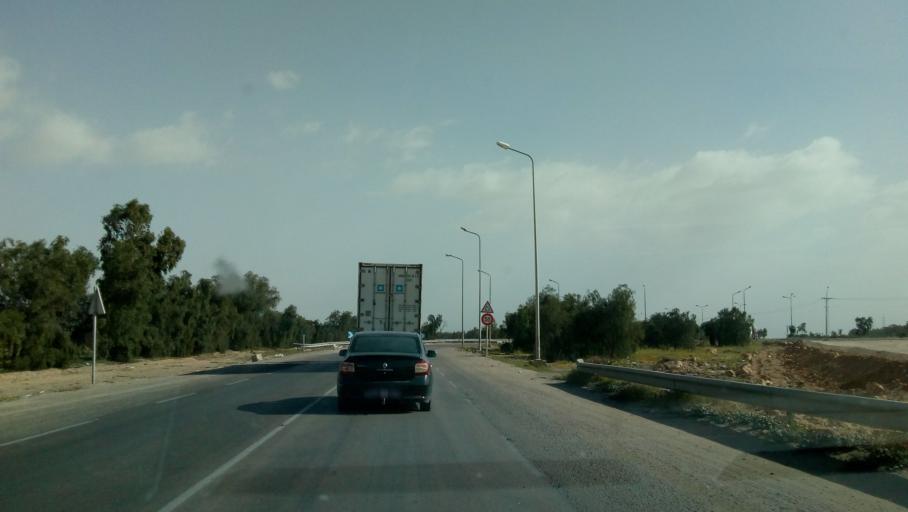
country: TN
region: Qabis
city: Gabes
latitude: 33.8874
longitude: 10.0196
